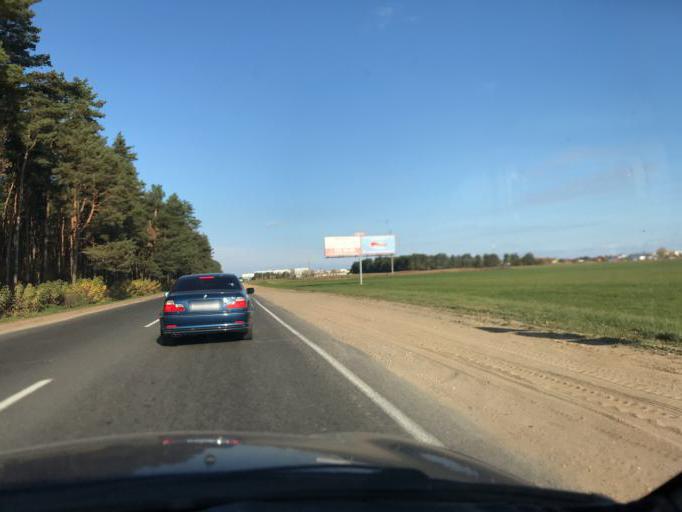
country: BY
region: Grodnenskaya
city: Lida
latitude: 53.8774
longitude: 25.2578
